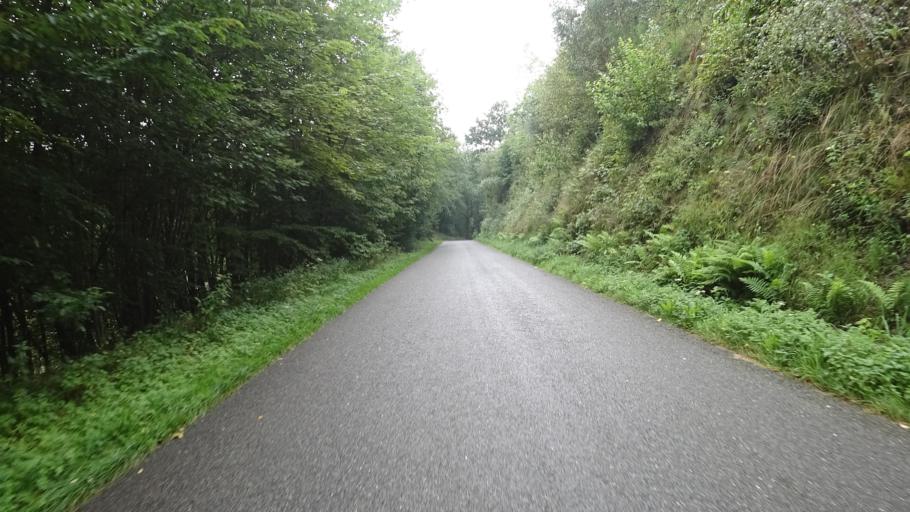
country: BE
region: Wallonia
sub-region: Province du Luxembourg
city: Chiny
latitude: 49.7899
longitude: 5.3751
